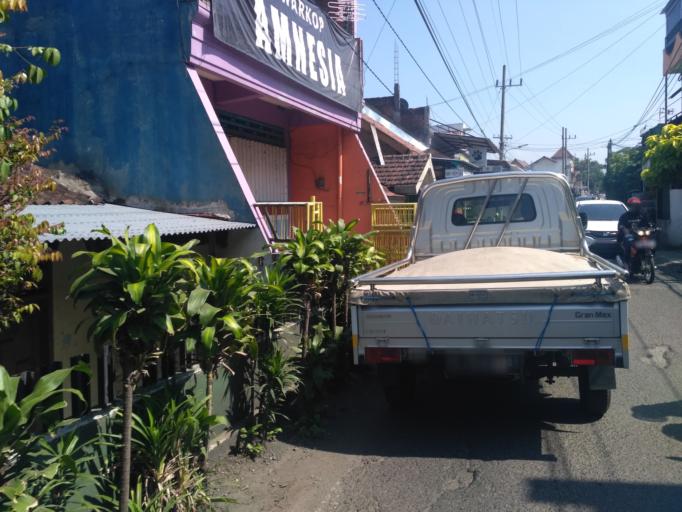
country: ID
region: East Java
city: Malang
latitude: -7.9378
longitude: 112.6210
